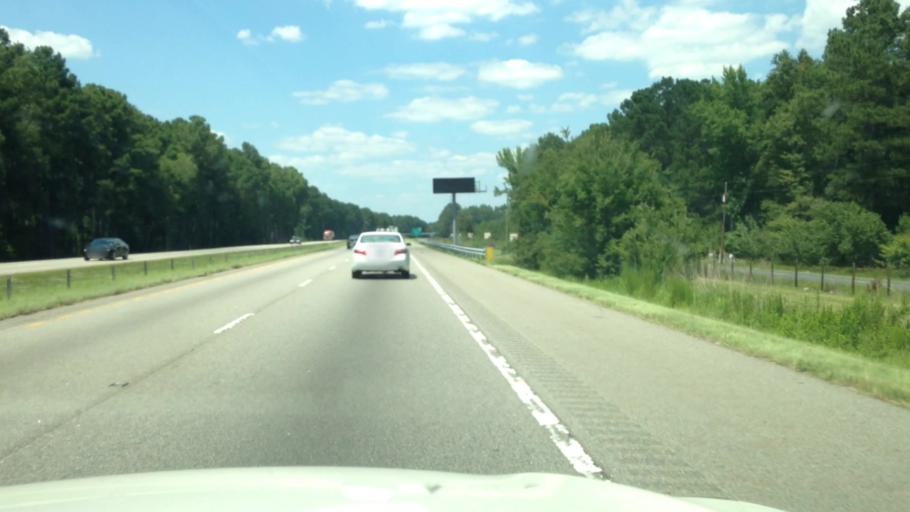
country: US
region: North Carolina
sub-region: Cumberland County
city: Hope Mills
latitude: 34.8987
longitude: -78.9584
